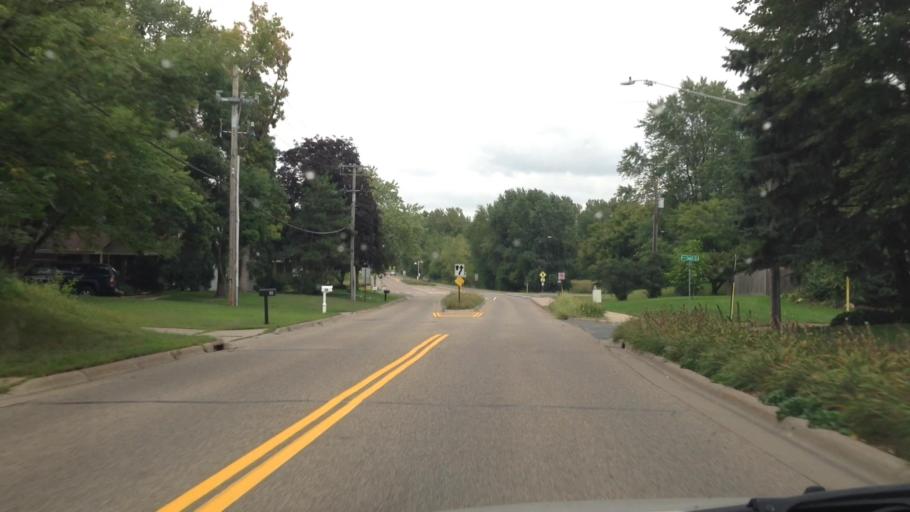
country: US
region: Minnesota
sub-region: Hennepin County
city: Saint Louis Park
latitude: 44.9771
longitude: -93.3805
